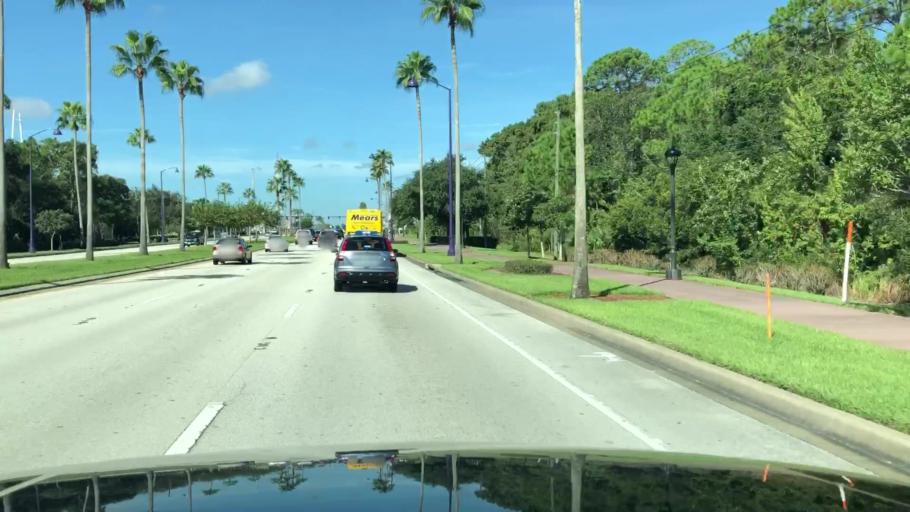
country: US
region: Florida
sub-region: Osceola County
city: Celebration
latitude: 28.3330
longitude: -81.5084
